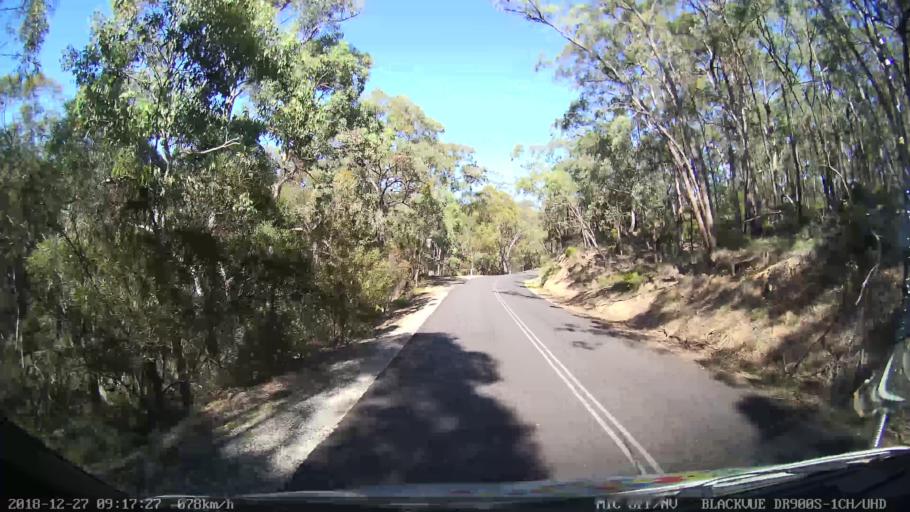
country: AU
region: New South Wales
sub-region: Lithgow
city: Portland
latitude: -33.1357
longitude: 150.0504
